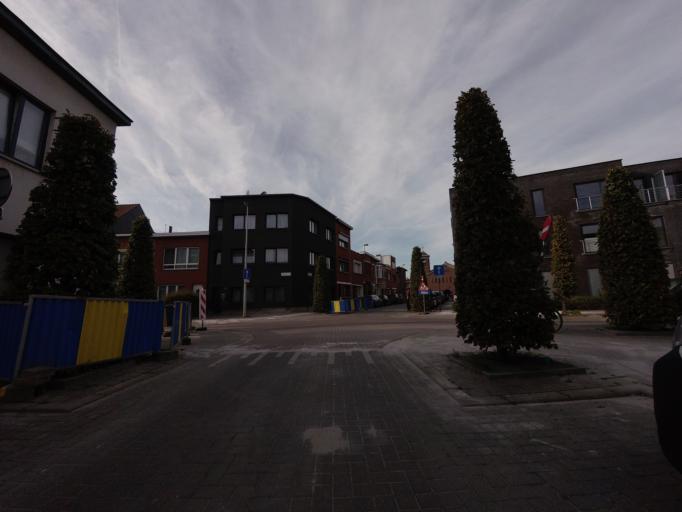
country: BE
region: Flanders
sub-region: Provincie Antwerpen
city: Antwerpen
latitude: 51.2292
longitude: 4.4490
